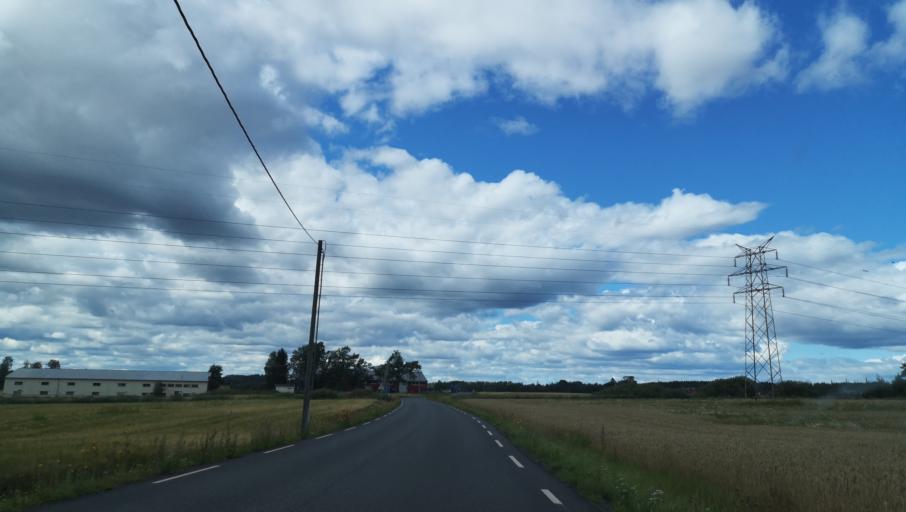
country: NO
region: Akershus
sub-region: Ski
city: Ski
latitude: 59.7080
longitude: 10.8895
